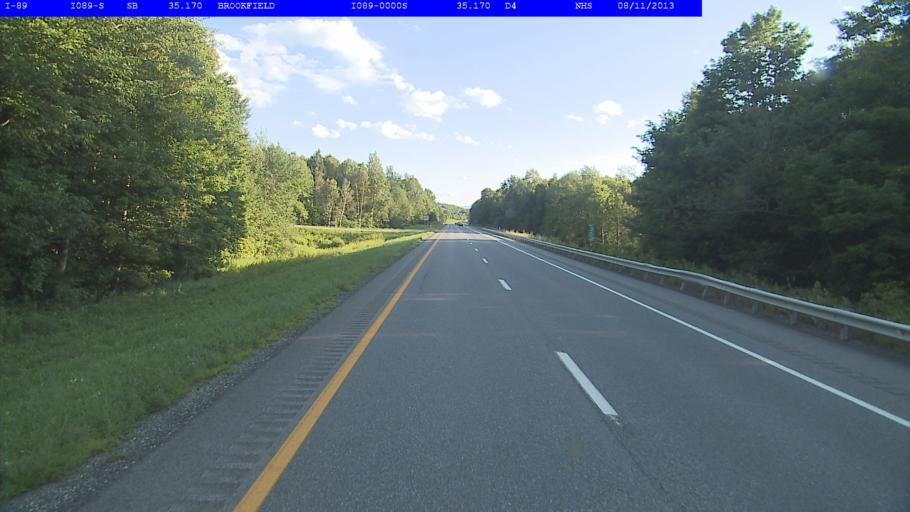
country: US
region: Vermont
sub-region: Orange County
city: Randolph
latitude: 44.0062
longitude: -72.6216
